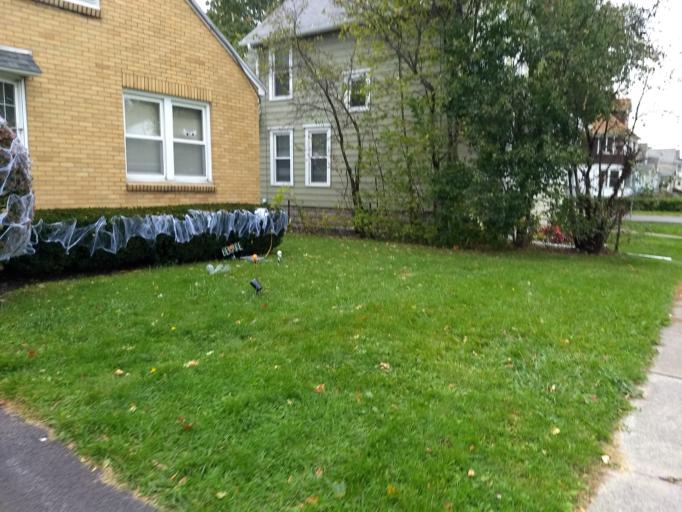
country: US
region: New York
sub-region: Onondaga County
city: Mattydale
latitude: 43.0787
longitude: -76.1516
